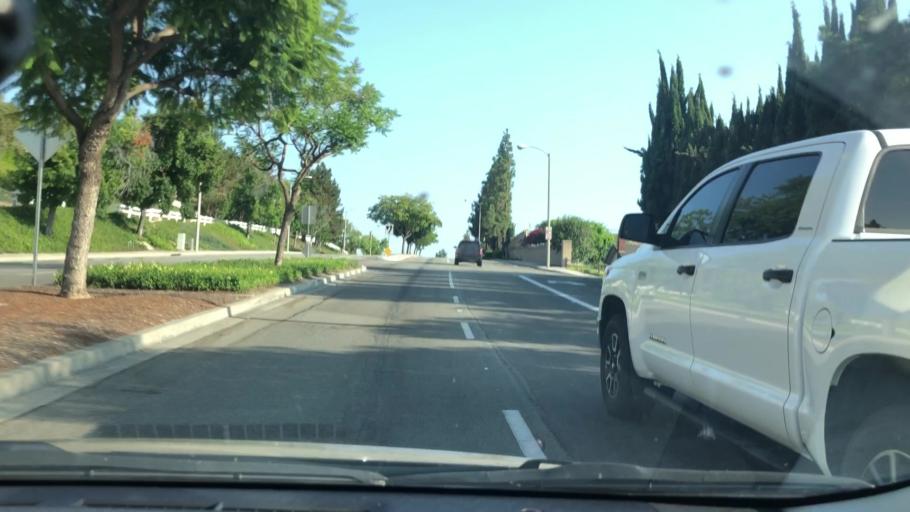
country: US
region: California
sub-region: Orange County
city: Yorba Linda
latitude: 33.8785
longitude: -117.7851
